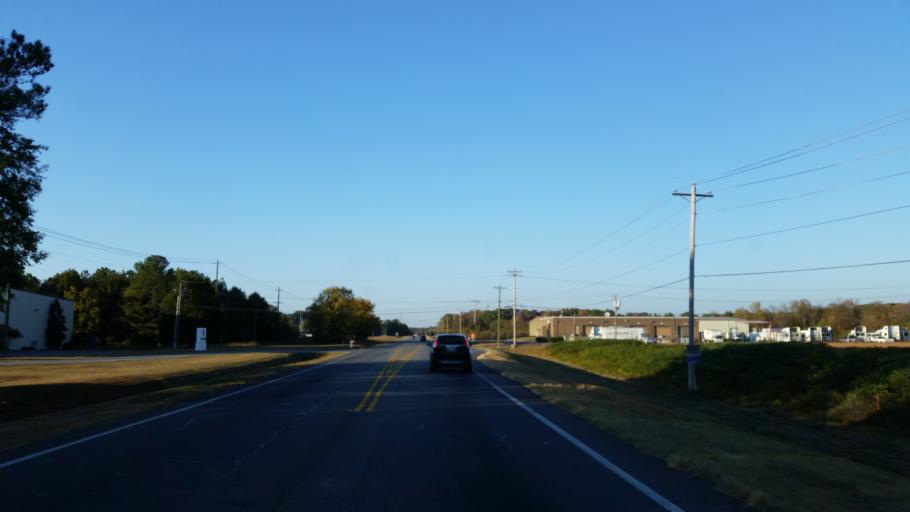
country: US
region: Georgia
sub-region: Gordon County
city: Calhoun
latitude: 34.4606
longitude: -84.9344
